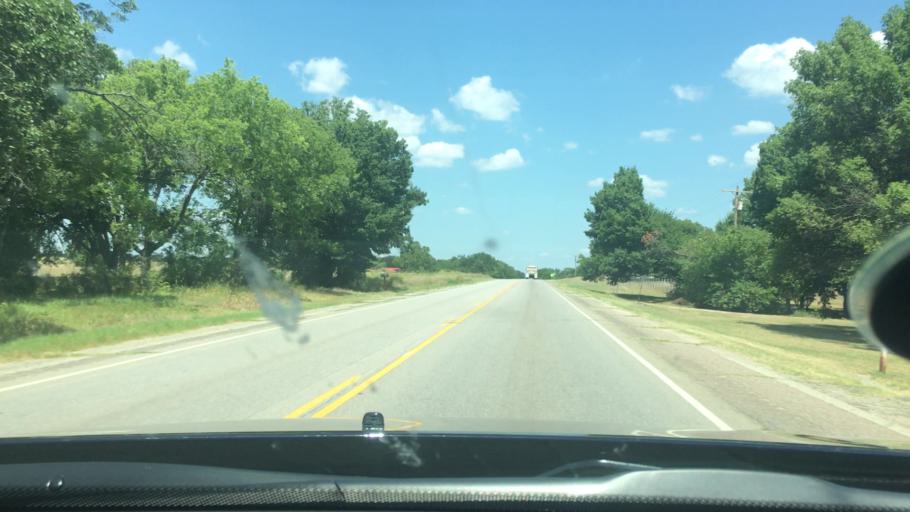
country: US
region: Oklahoma
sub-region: Marshall County
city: Oakland
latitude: 34.1446
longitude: -96.8066
